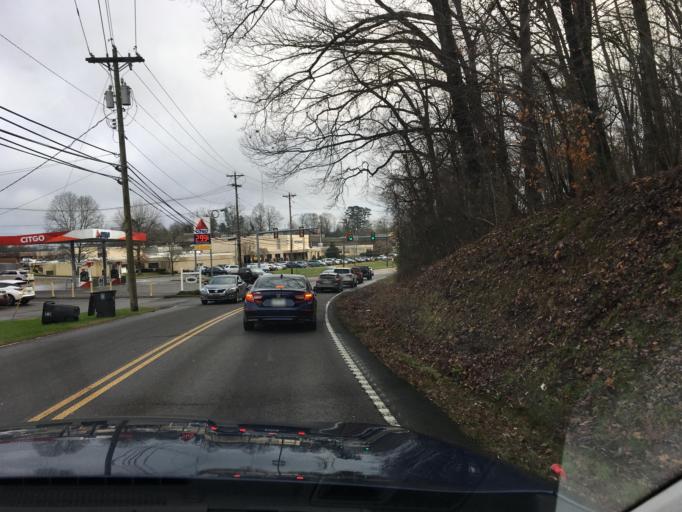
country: US
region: Tennessee
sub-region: McMinn County
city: Athens
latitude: 35.4410
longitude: -84.6097
